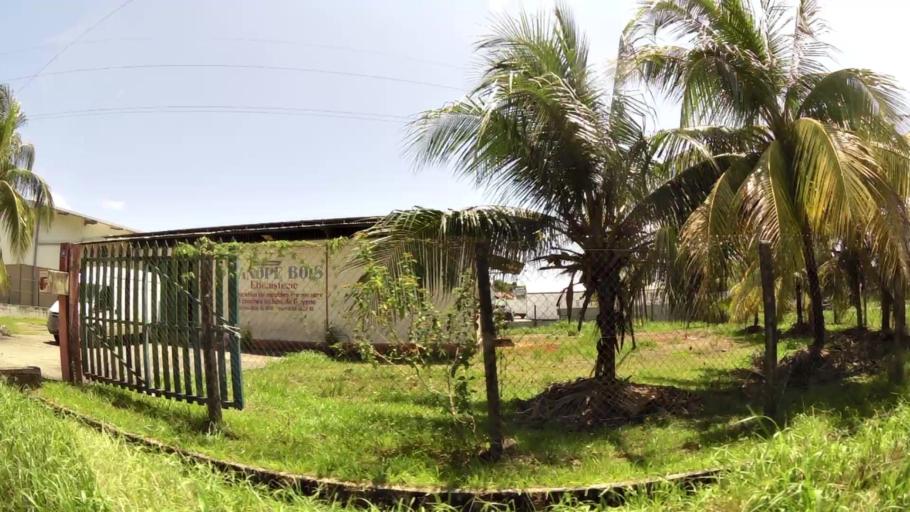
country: GF
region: Guyane
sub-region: Guyane
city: Cayenne
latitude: 4.9014
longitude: -52.3179
